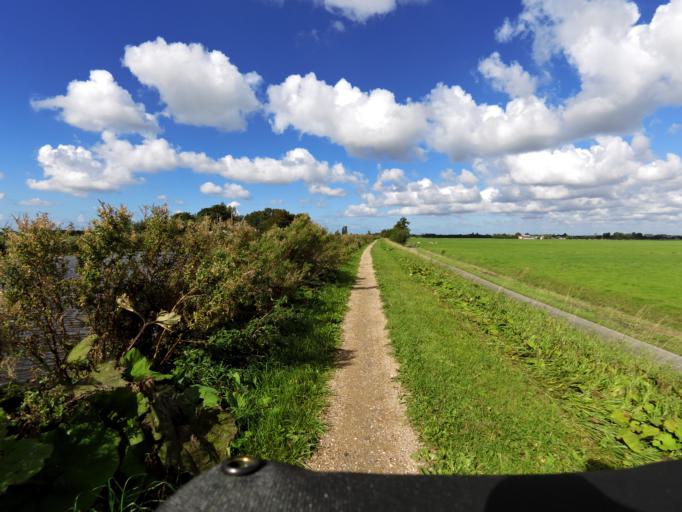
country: NL
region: South Holland
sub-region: Gemeente Vlaardingen
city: Vlaardingen
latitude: 51.9571
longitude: 4.3152
